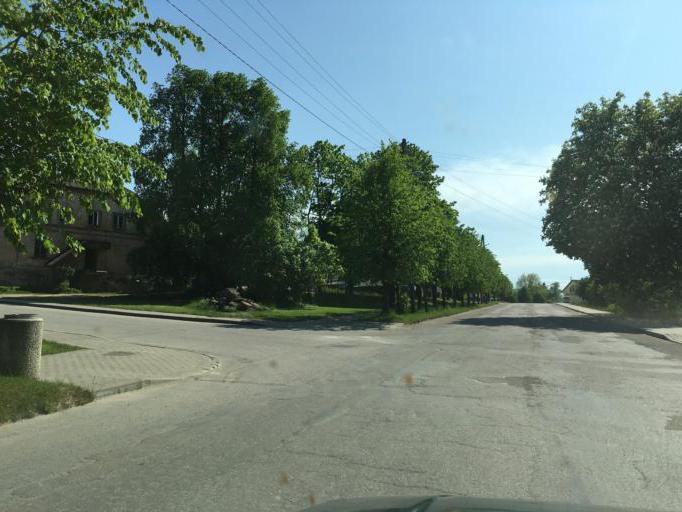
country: LV
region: Dundaga
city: Dundaga
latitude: 57.5113
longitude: 22.3520
